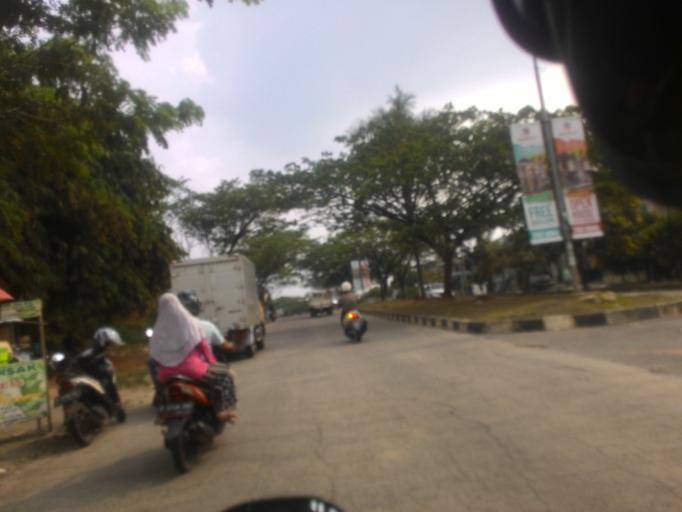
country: ID
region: West Java
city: Depok
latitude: -6.4286
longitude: 106.8271
